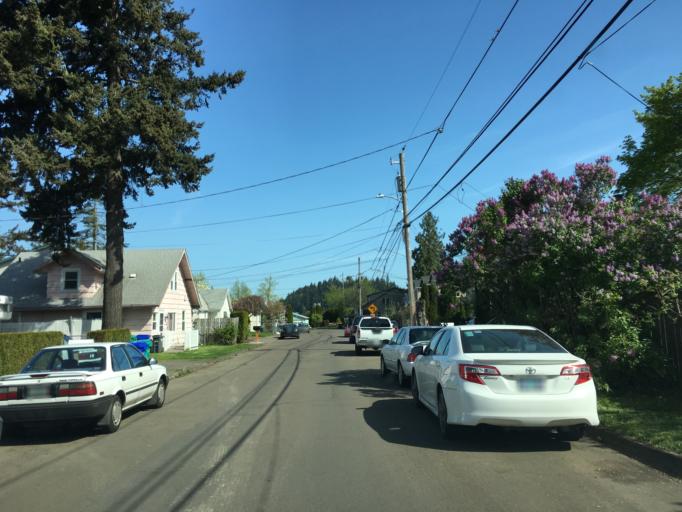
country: US
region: Oregon
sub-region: Multnomah County
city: Lents
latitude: 45.5287
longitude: -122.5669
